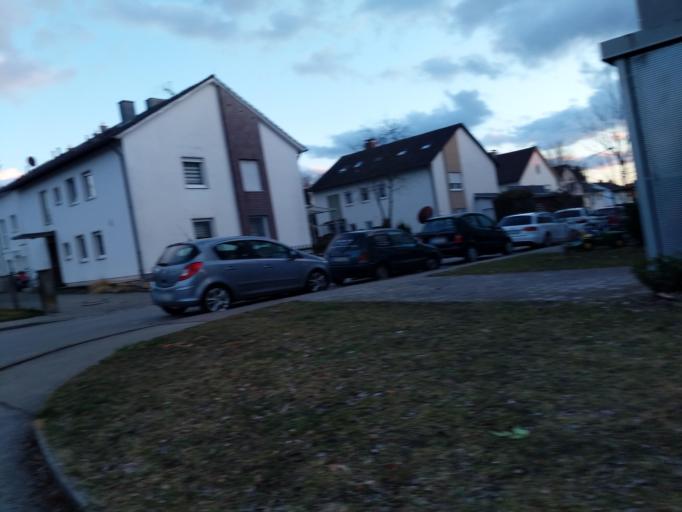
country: DE
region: Bavaria
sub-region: Swabia
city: Bobingen
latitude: 48.2776
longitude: 10.8451
